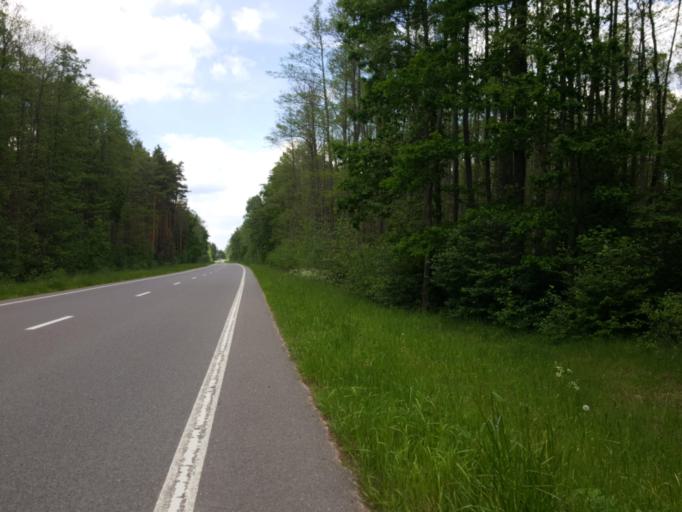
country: BY
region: Brest
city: Kamyanyuki
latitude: 52.5375
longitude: 23.6546
